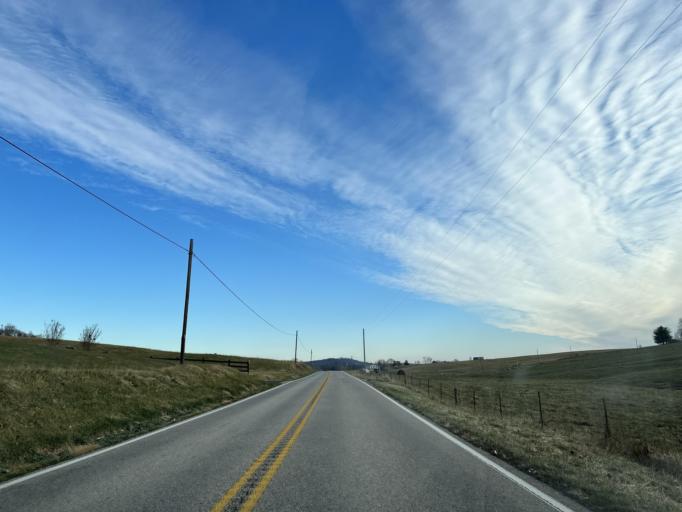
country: US
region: Virginia
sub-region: Rockingham County
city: Bridgewater
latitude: 38.3491
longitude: -79.0339
